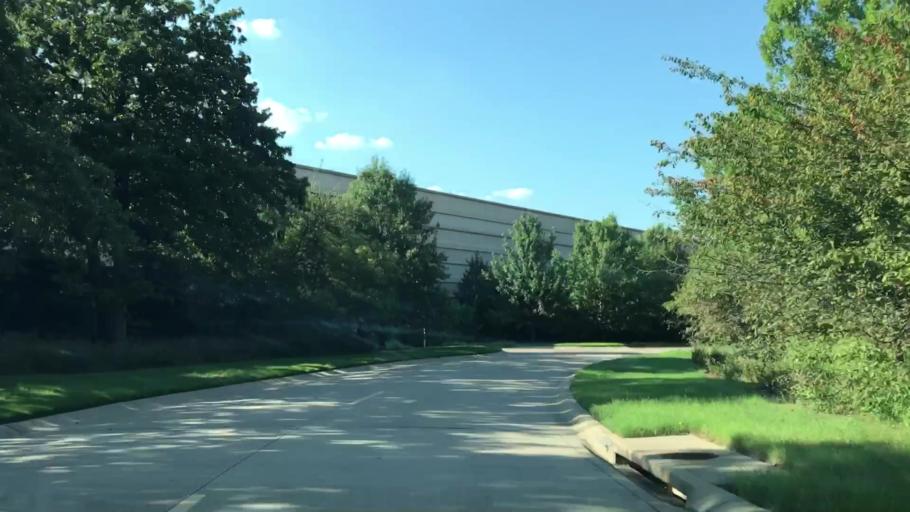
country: US
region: Texas
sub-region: Denton County
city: Trophy Club
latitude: 32.9838
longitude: -97.1861
